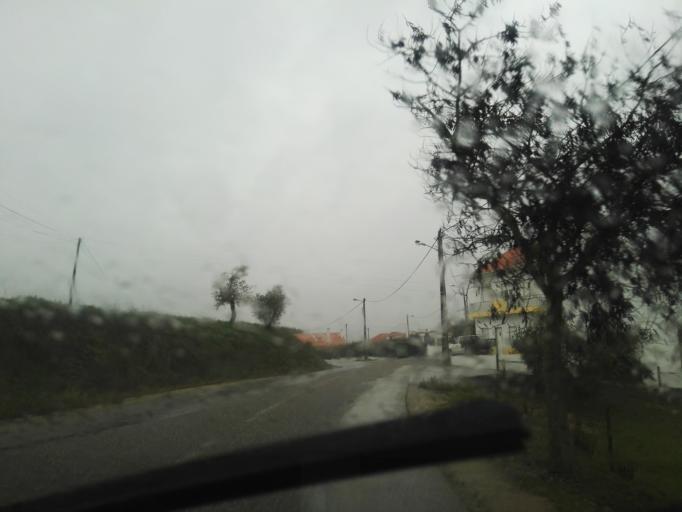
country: PT
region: Santarem
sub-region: Santarem
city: Santarem
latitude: 39.2874
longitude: -8.7763
